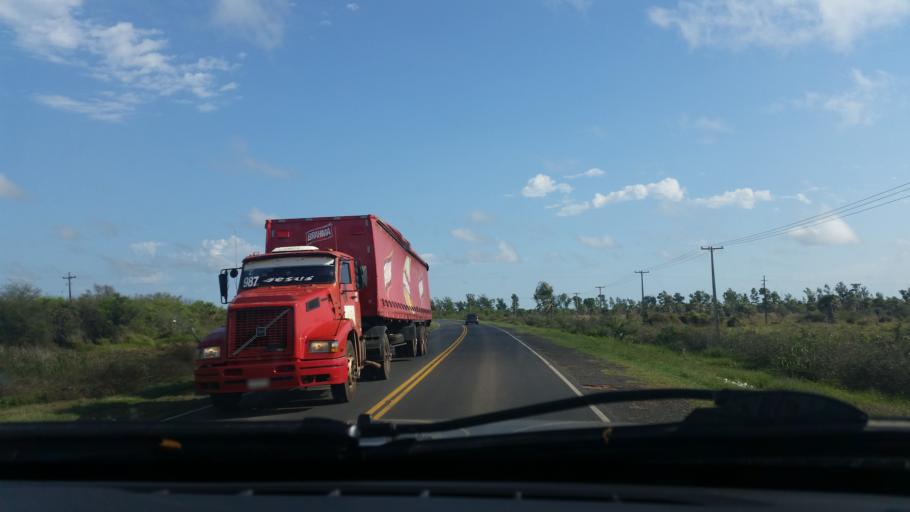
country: PY
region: Presidente Hayes
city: Benjamin Aceval
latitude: -24.9406
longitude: -57.5547
